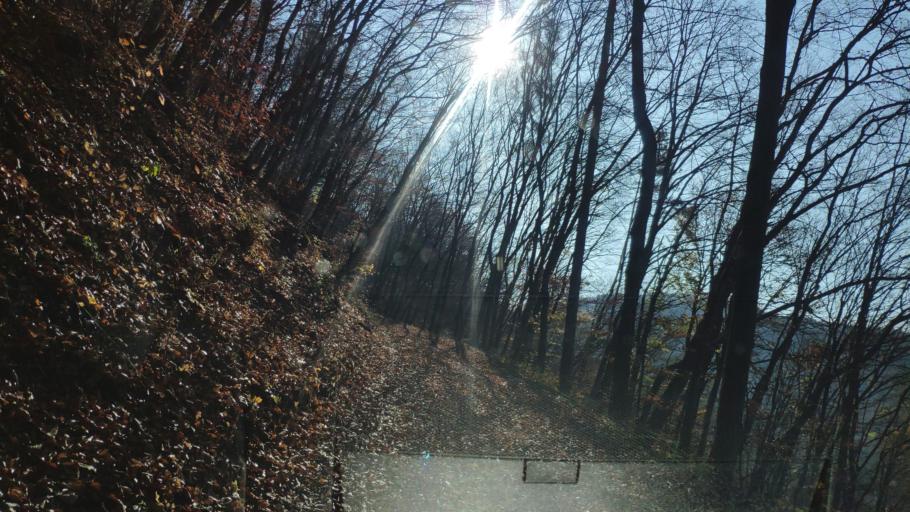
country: SK
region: Presovsky
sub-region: Okres Presov
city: Presov
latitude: 48.8976
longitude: 21.2076
